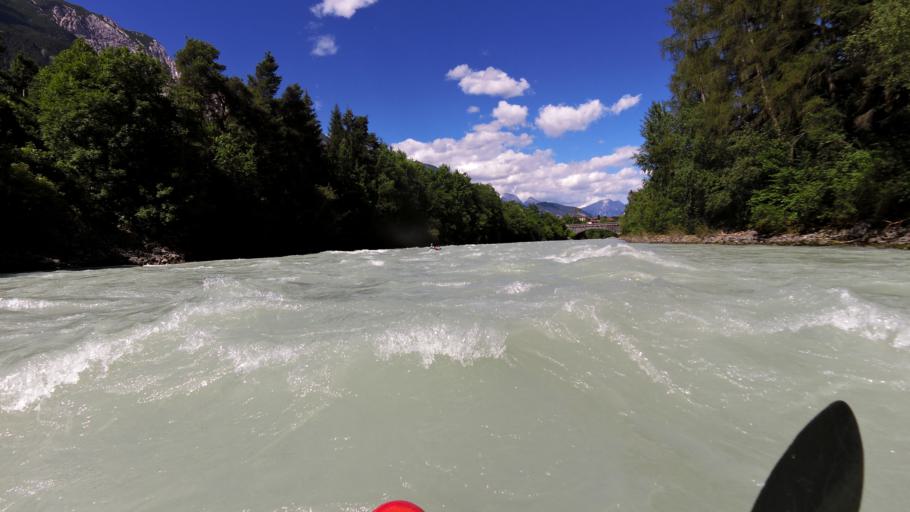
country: AT
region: Tyrol
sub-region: Politischer Bezirk Imst
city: Roppen
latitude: 47.2140
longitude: 10.8119
